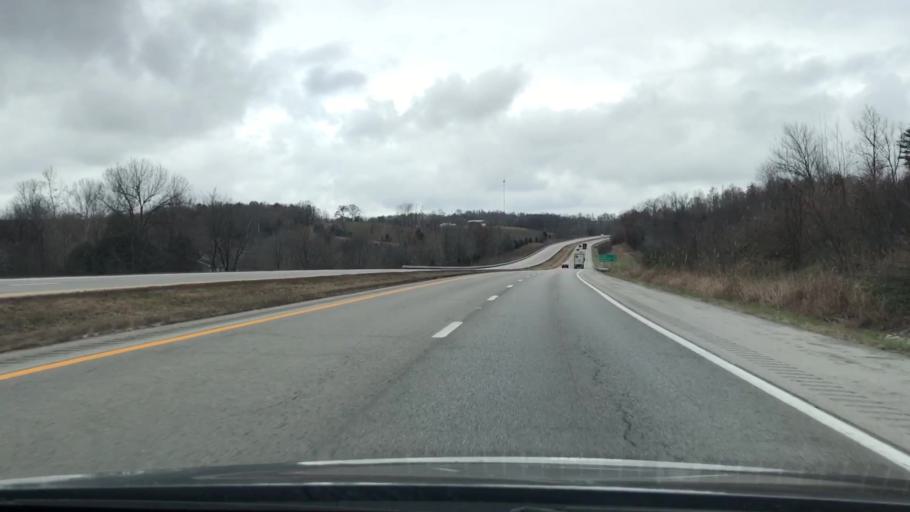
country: US
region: Kentucky
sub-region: Christian County
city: Hopkinsville
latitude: 36.9102
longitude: -87.4740
